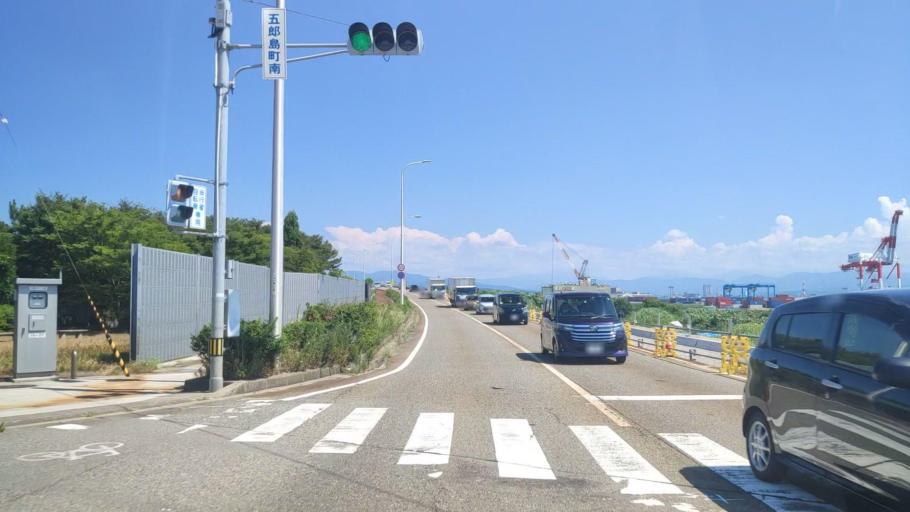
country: JP
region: Ishikawa
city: Kanazawa-shi
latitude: 36.6172
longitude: 136.6220
